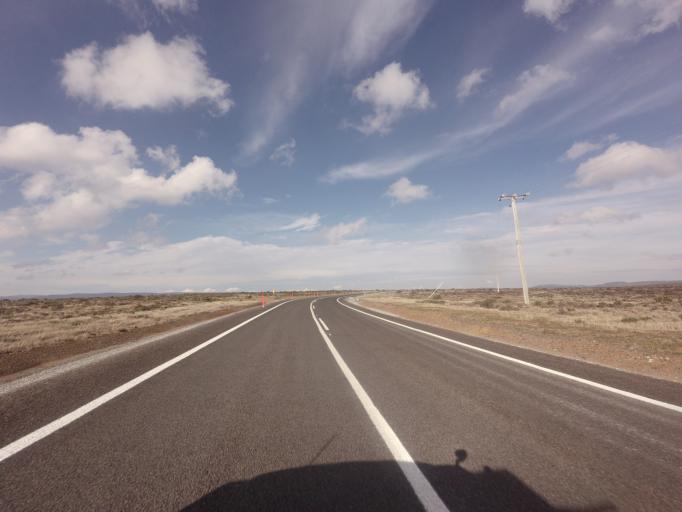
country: AU
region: Tasmania
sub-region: Meander Valley
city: Deloraine
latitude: -41.9118
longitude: 146.6845
